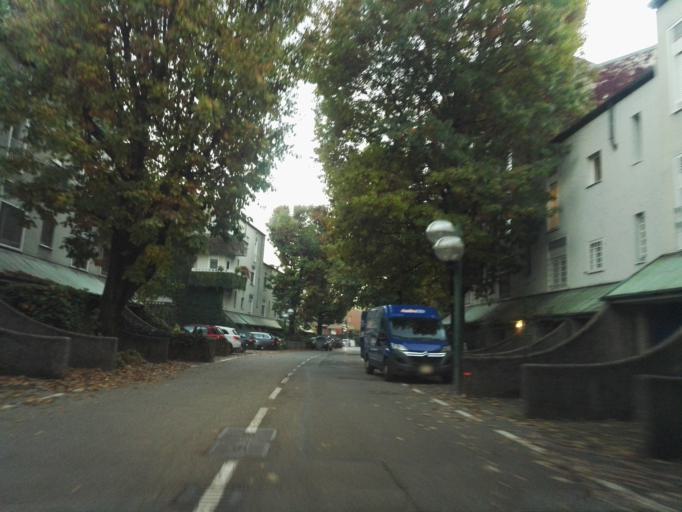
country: IT
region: Lombardy
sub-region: Citta metropolitana di Milano
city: San Bovio-San Felice
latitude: 45.4690
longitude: 9.3087
